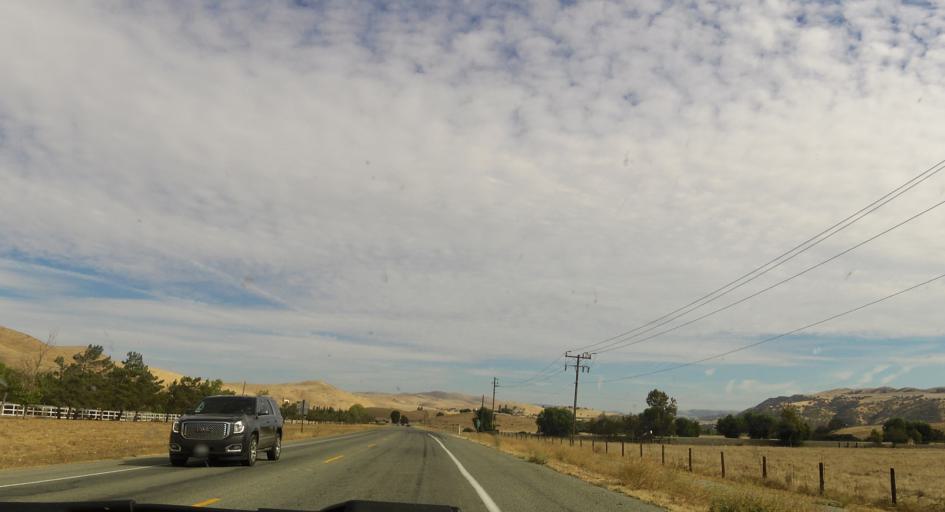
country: US
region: California
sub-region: San Benito County
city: Ridgemark
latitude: 36.7978
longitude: -121.3327
